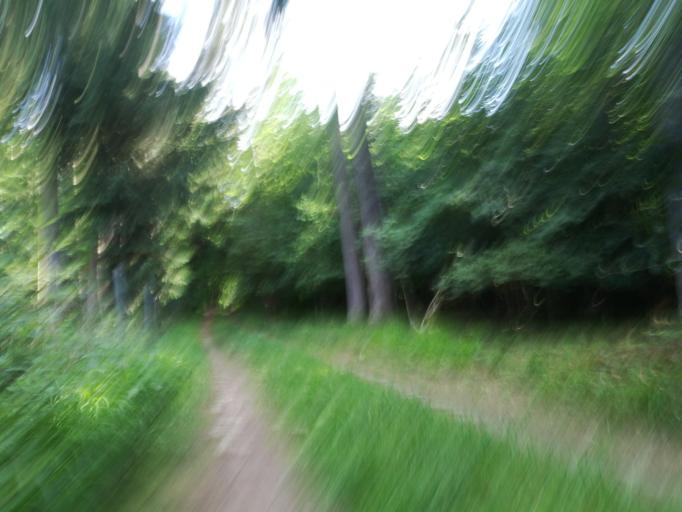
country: DE
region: Bavaria
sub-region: Regierungsbezirk Mittelfranken
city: Obermichelbach
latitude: 49.5059
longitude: 10.9193
